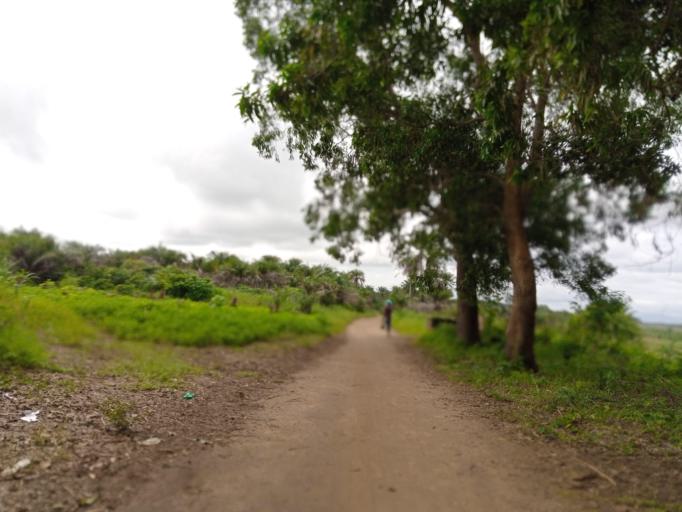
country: SL
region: Northern Province
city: Masoyila
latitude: 8.5857
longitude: -13.1952
